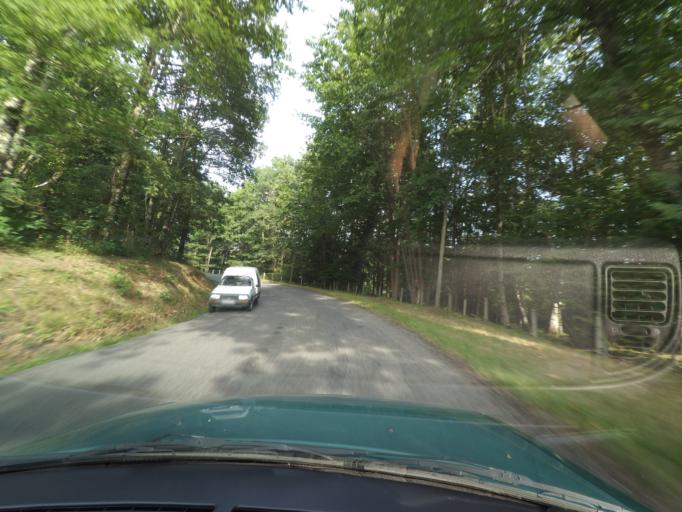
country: FR
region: Limousin
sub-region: Departement de la Haute-Vienne
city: Rochechouart
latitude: 45.8017
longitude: 0.8671
